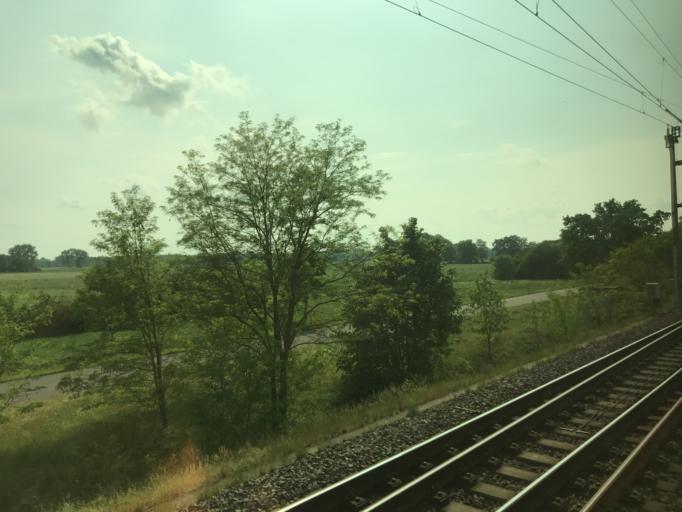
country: DE
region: Brandenburg
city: Nennhausen
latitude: 52.5991
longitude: 12.5181
